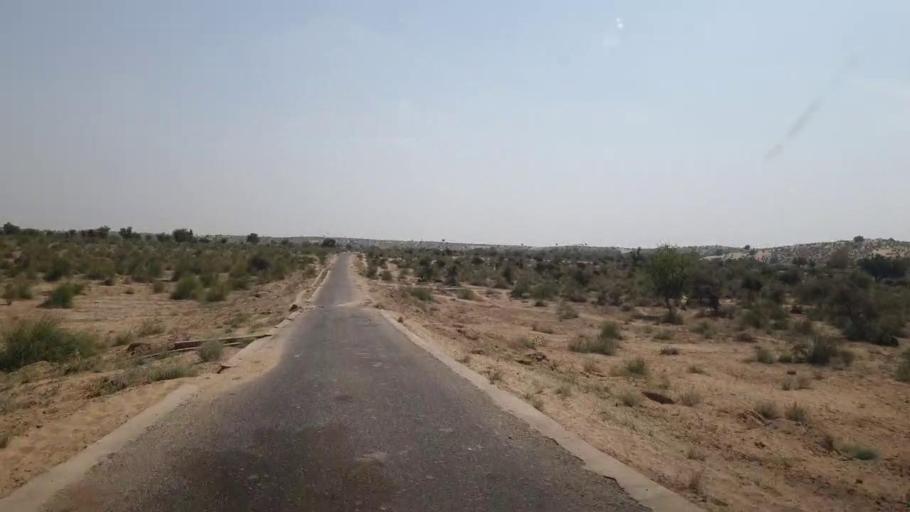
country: PK
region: Sindh
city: Islamkot
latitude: 25.0762
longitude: 70.7398
